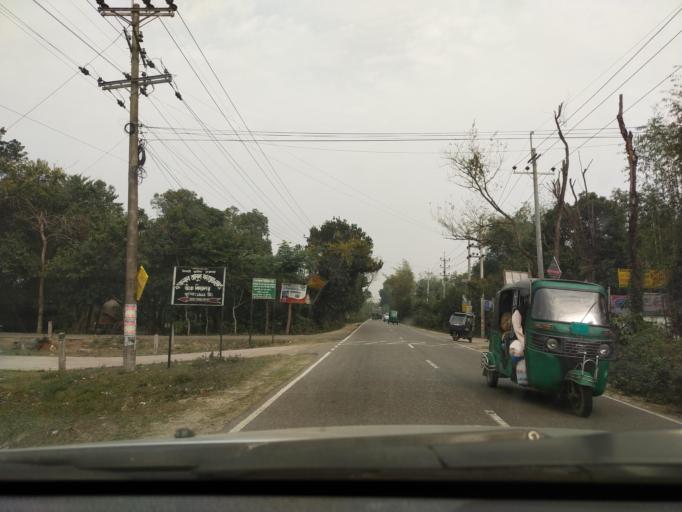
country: BD
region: Dhaka
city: Narsingdi
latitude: 24.0126
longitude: 90.7372
